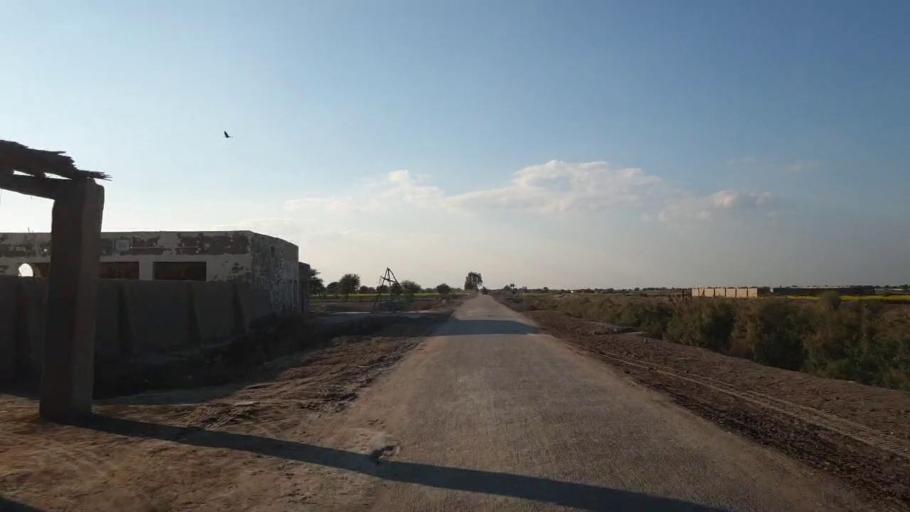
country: PK
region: Sindh
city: Shahpur Chakar
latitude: 26.1463
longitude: 68.5350
